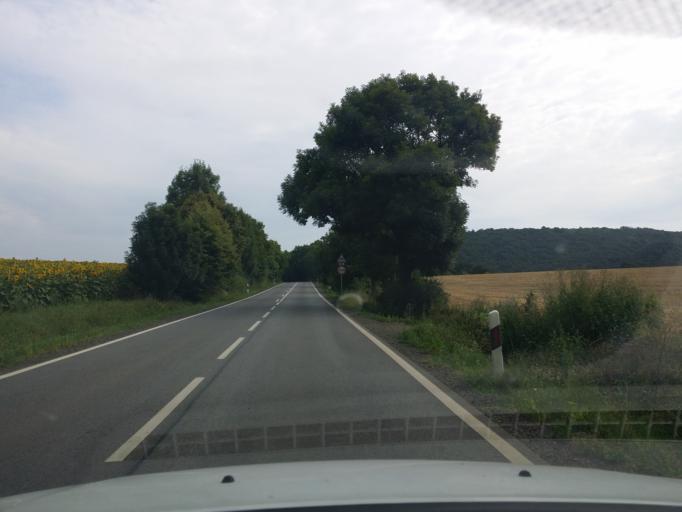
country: HU
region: Pest
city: Acsa
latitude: 47.7846
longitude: 19.3639
